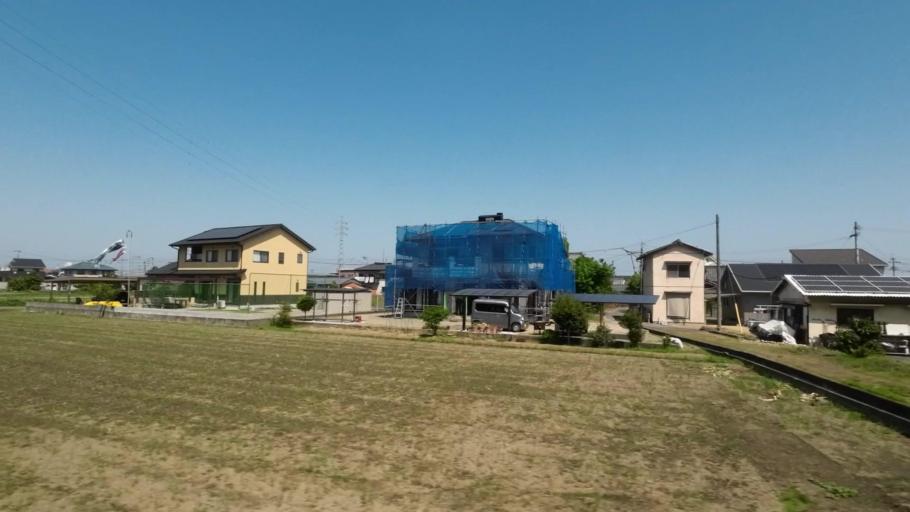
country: JP
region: Ehime
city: Niihama
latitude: 33.9593
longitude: 133.3074
